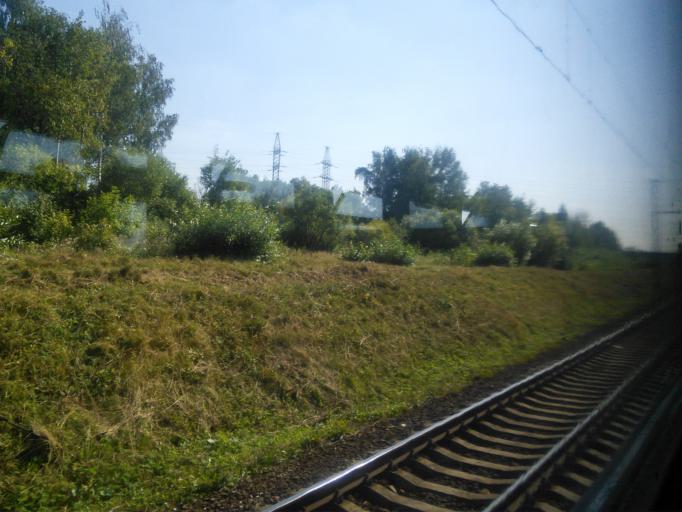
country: RU
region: Moscow
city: Tsaritsyno
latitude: 55.6090
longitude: 37.6381
